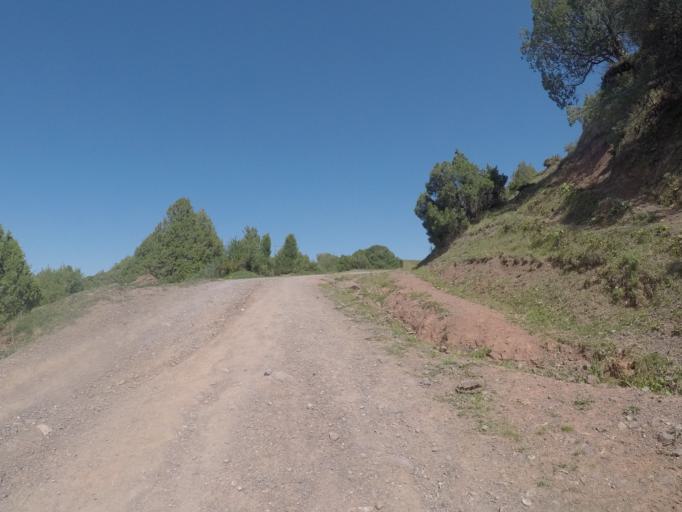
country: KG
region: Chuy
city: Bishkek
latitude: 42.6464
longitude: 74.5597
